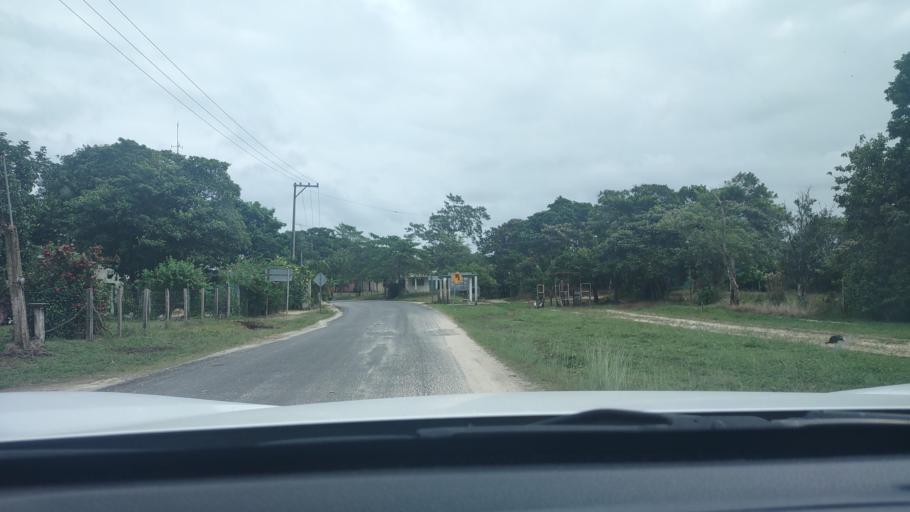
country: MX
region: Veracruz
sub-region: Moloacan
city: Cuichapa
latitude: 17.8996
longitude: -94.2978
